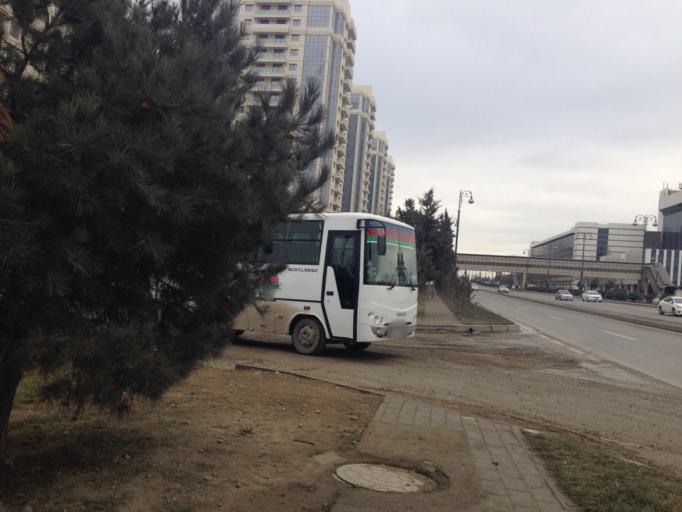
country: AZ
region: Baki
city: Baku
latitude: 40.4165
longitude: 49.9066
